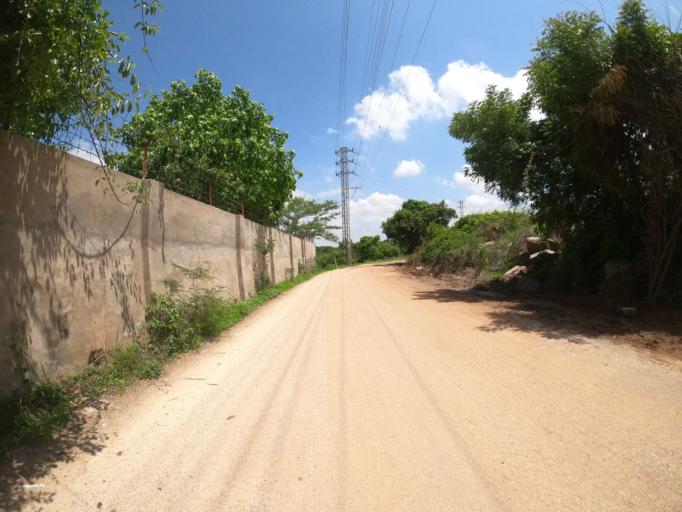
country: IN
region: Telangana
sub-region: Medak
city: Serilingampalle
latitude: 17.3752
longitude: 78.3210
